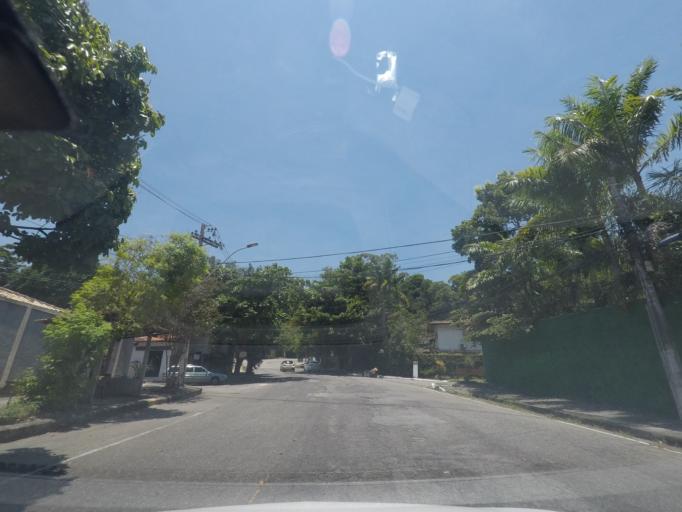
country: BR
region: Rio de Janeiro
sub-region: Niteroi
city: Niteroi
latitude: -22.9152
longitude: -43.0653
